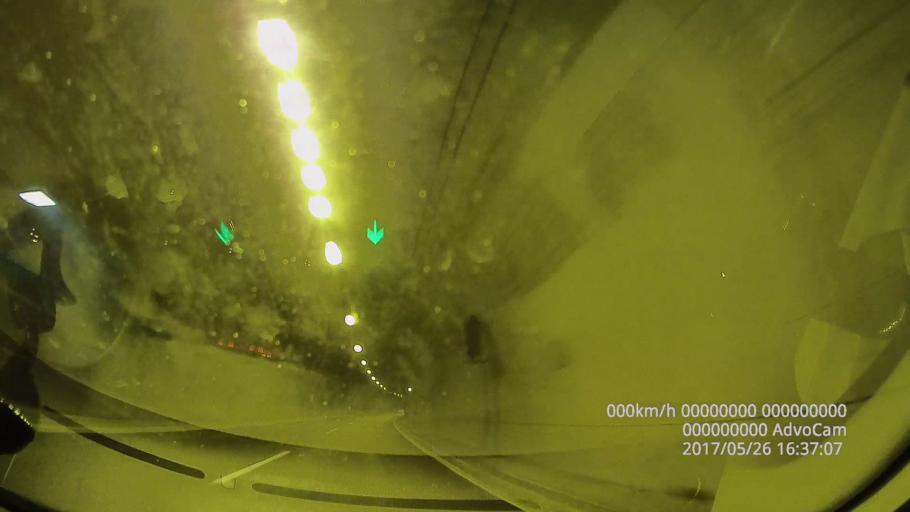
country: GR
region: Central Greece
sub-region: Nomos Fthiotidos
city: Rodhitsa
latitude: 38.8891
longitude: 22.4755
